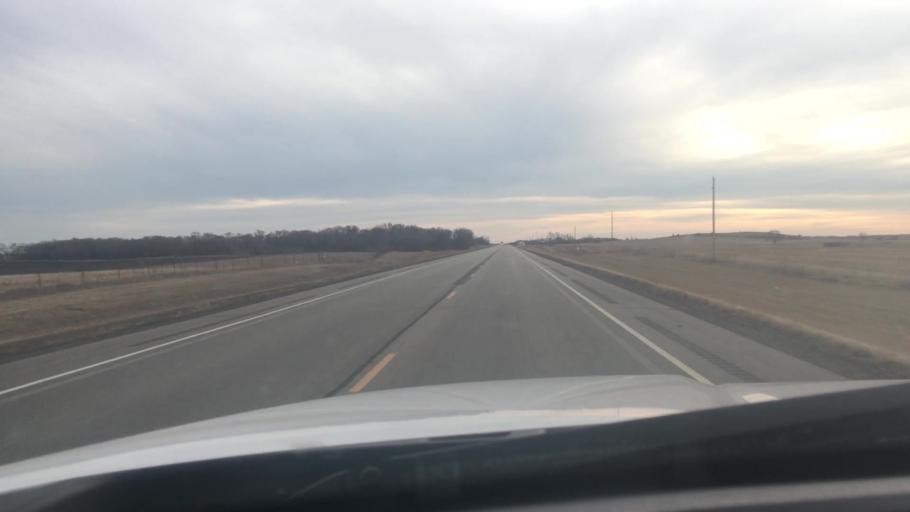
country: US
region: Minnesota
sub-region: Otter Tail County
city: Perham
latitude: 46.3351
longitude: -95.7185
